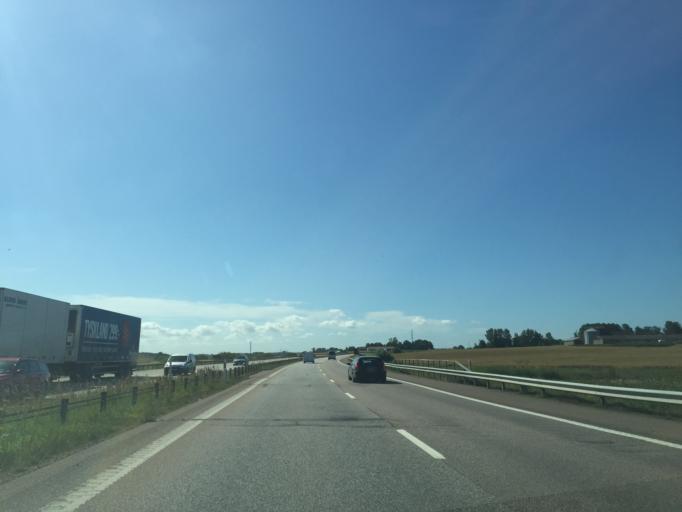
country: SE
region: Skane
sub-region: Angelholms Kommun
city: Strovelstorp
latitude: 56.1488
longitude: 12.8444
